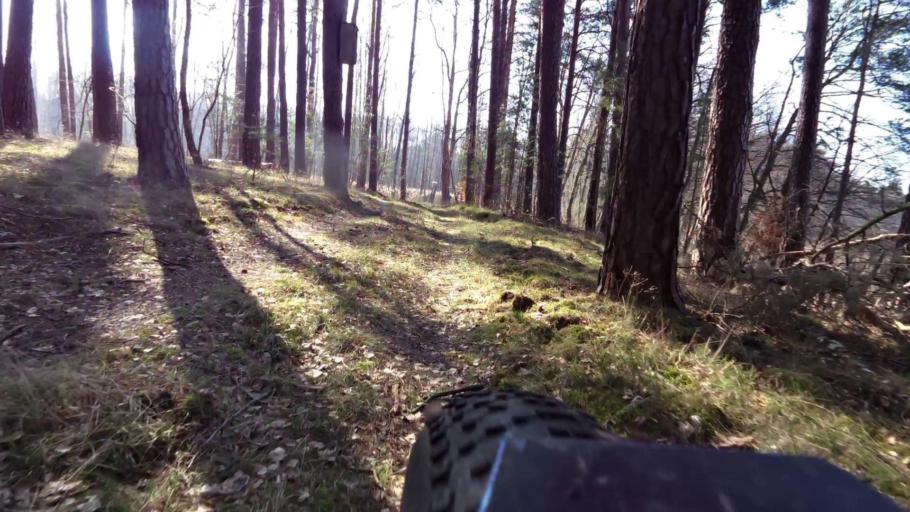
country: PL
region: Lubusz
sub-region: Powiat krosnienski
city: Maszewo
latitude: 52.2133
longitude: 14.9529
